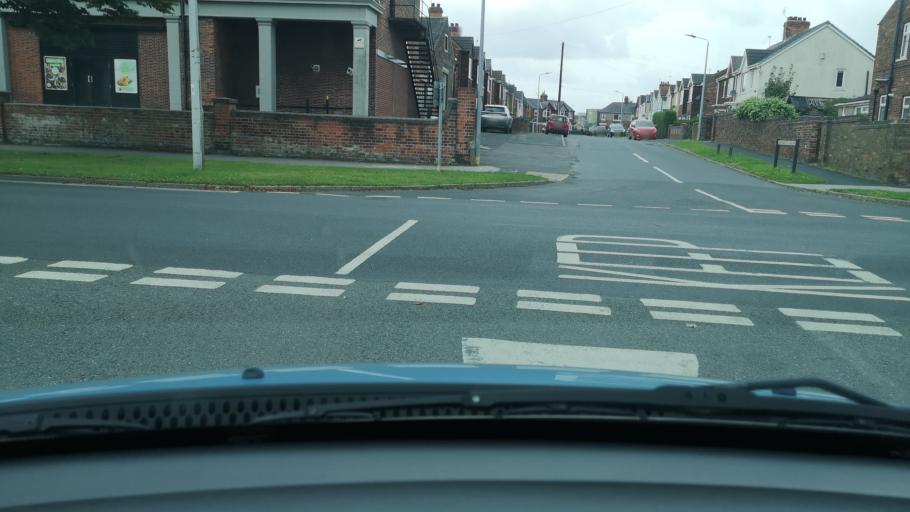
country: GB
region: England
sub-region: North Lincolnshire
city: Scunthorpe
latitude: 53.5914
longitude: -0.6610
